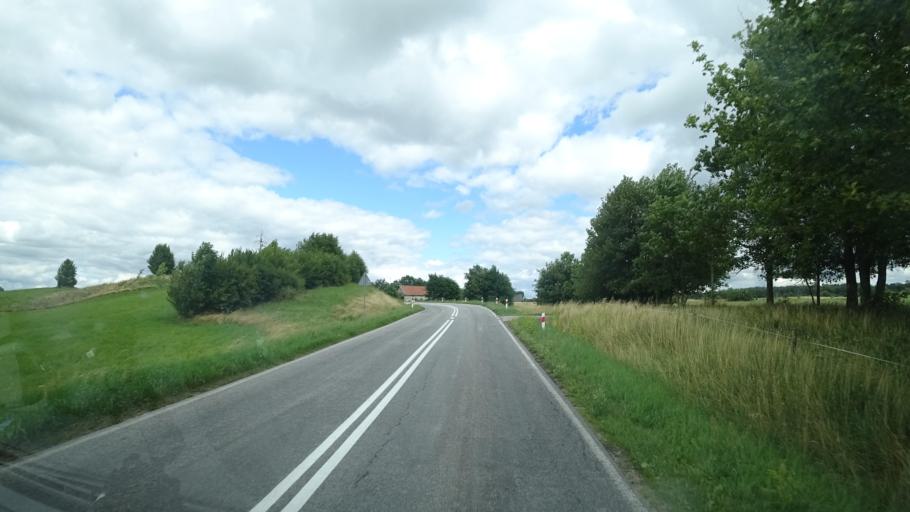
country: PL
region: Warmian-Masurian Voivodeship
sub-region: Powiat goldapski
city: Goldap
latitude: 54.2183
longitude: 22.2280
